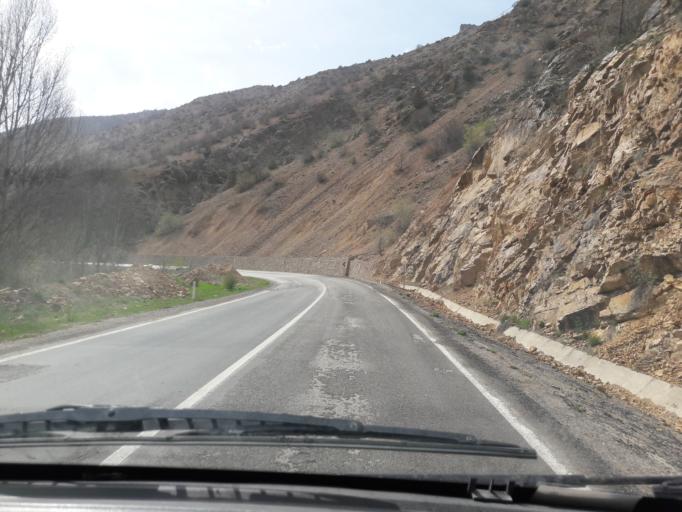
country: TR
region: Gumushane
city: Kale
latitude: 40.3942
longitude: 39.5900
